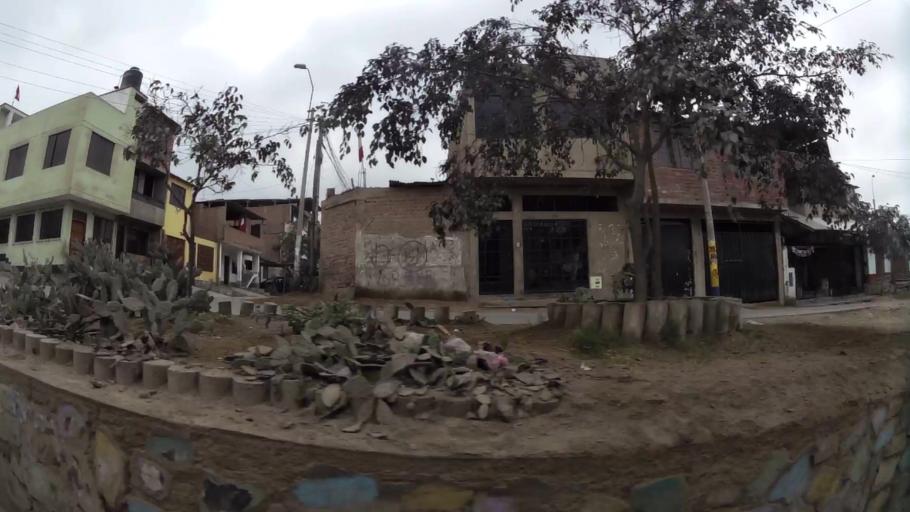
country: PE
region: Lima
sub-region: Lima
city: Surco
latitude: -12.1386
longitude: -76.9582
